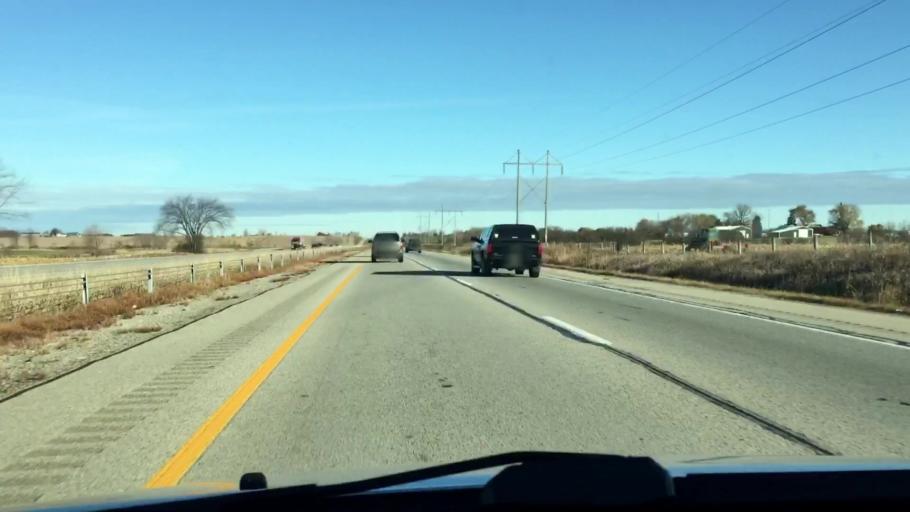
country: US
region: Wisconsin
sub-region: Fond du Lac County
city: Rosendale
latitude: 43.8743
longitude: -88.5840
